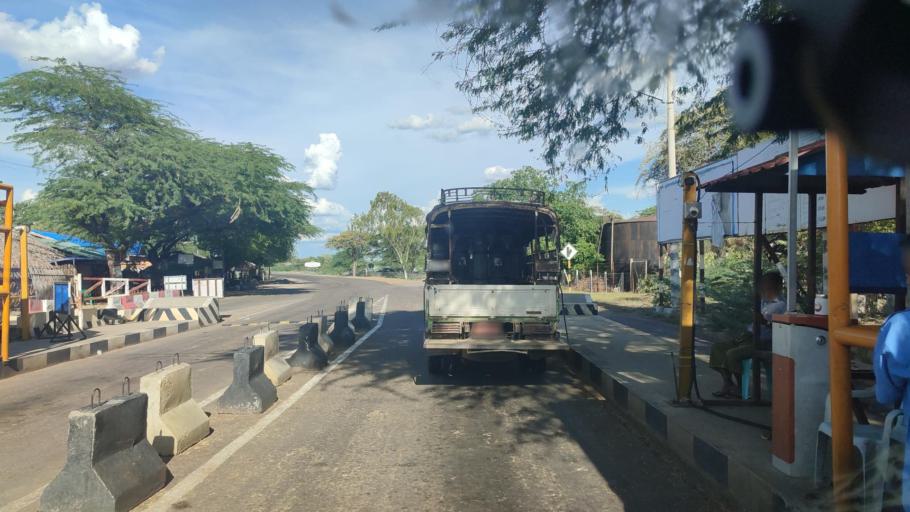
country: MM
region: Magway
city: Chauk
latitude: 20.8394
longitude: 94.8547
